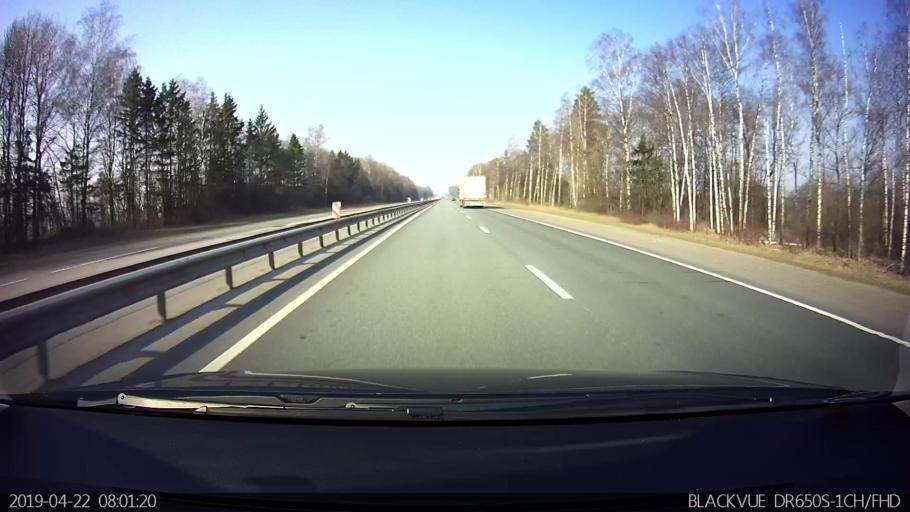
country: RU
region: Smolensk
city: Safonovo
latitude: 55.1234
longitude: 33.1006
